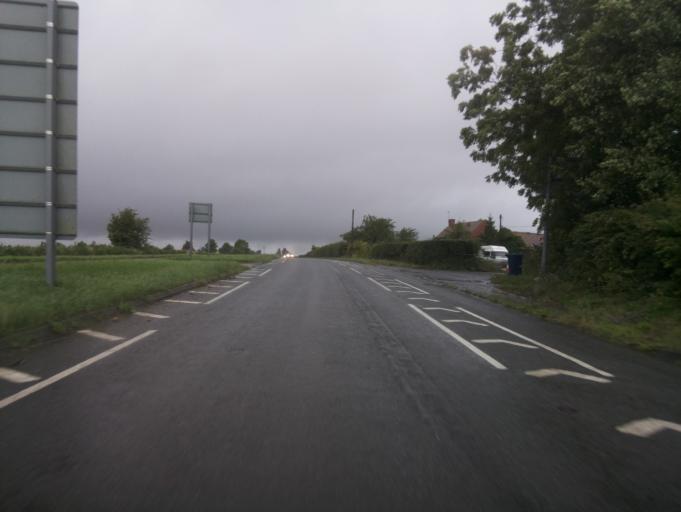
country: GB
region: England
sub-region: Gloucestershire
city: Tewkesbury
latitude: 51.9685
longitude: -2.1571
